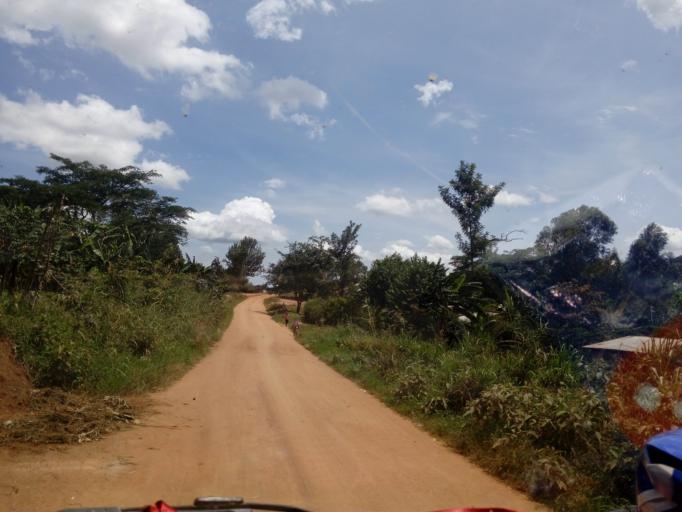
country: UG
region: Central Region
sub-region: Mubende District
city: Mubende
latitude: 0.4580
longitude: 31.6964
